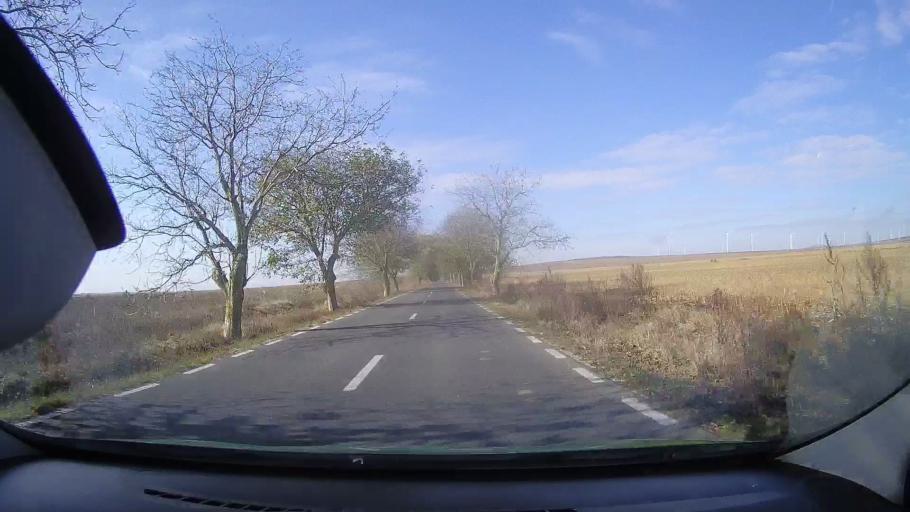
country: RO
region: Tulcea
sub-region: Comuna Bestepe
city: Bestepe
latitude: 45.0272
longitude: 29.0103
